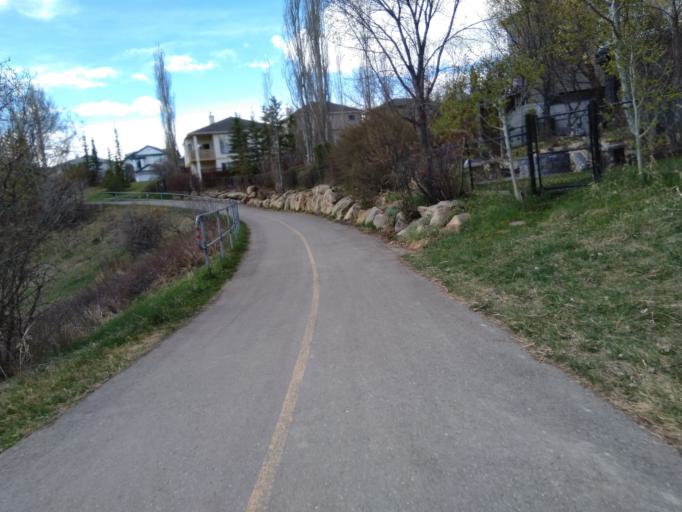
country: CA
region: Alberta
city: Calgary
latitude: 51.1225
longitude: -114.2378
